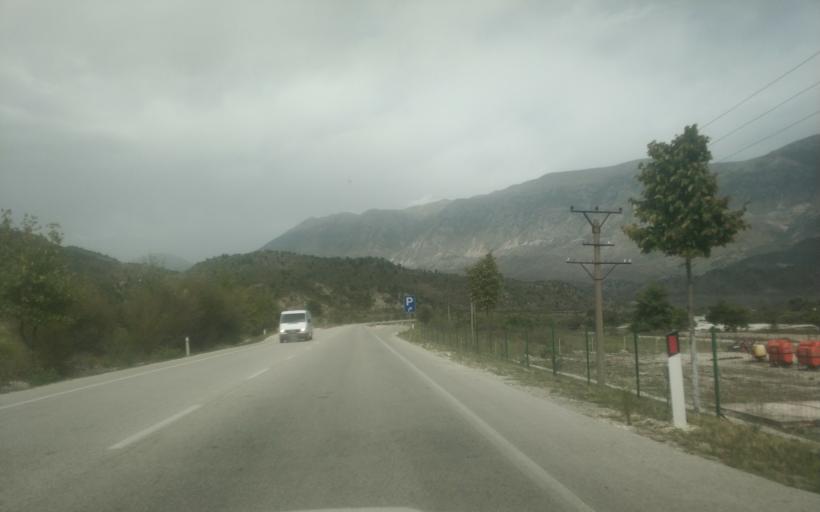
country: AL
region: Gjirokaster
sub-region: Rrethi i Gjirokastres
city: Picar
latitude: 40.1916
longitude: 20.0817
